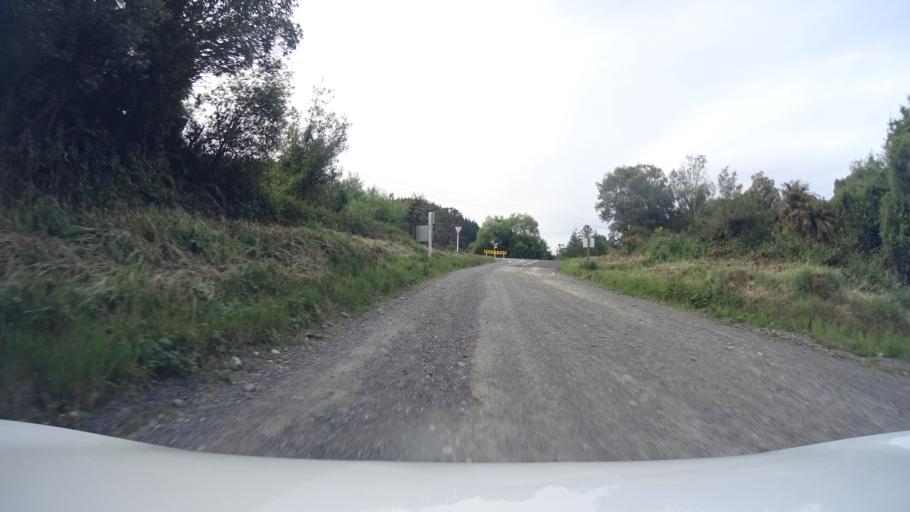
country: NZ
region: Bay of Plenty
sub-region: Rotorua District
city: Rotorua
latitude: -38.3219
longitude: 176.3731
